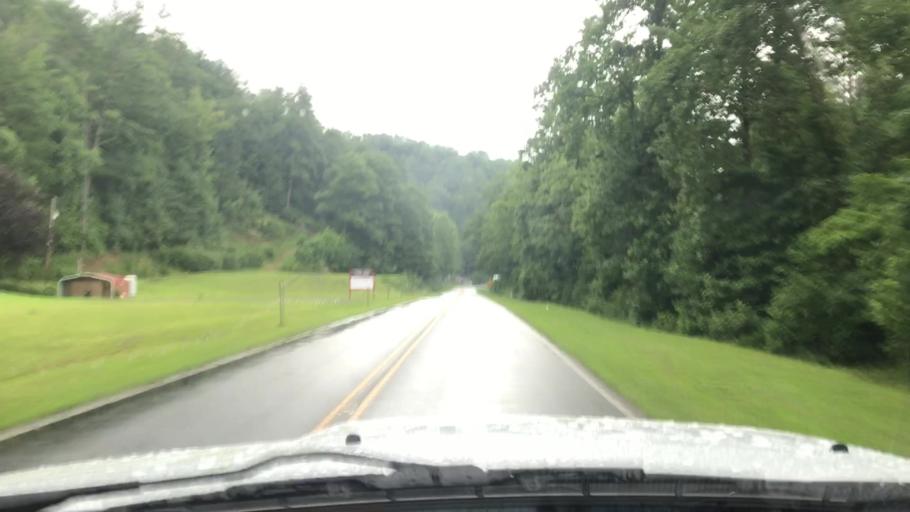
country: US
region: North Carolina
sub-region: Graham County
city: Robbinsville
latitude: 35.3959
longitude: -83.8658
